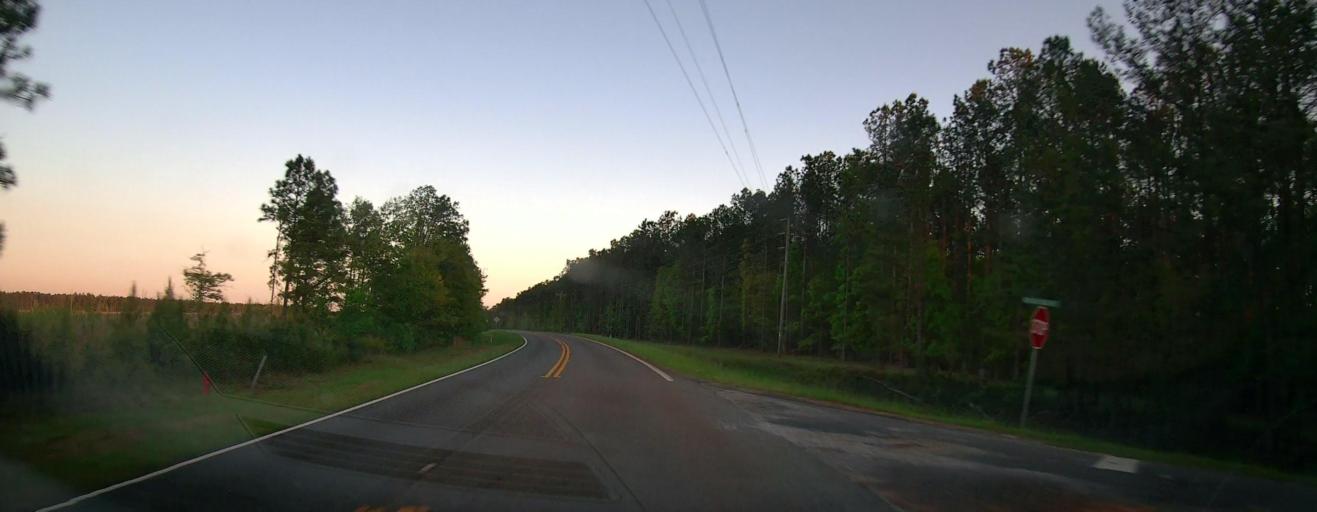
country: US
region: Georgia
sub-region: Marion County
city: Buena Vista
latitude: 32.3861
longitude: -84.5654
